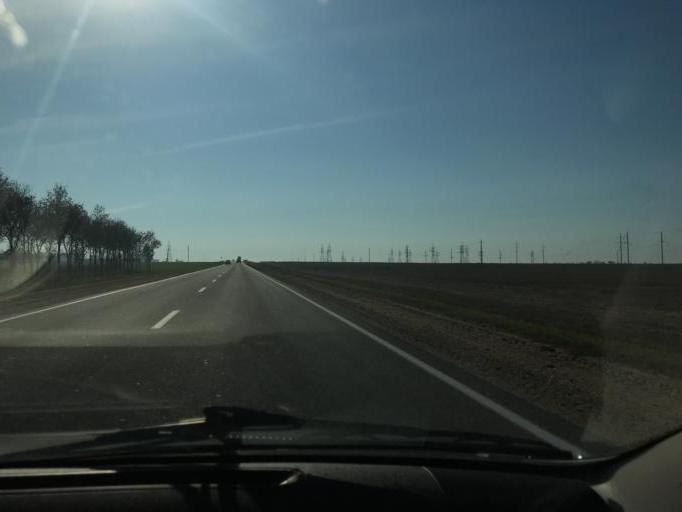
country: BY
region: Minsk
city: Salihorsk
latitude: 52.8671
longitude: 27.4671
